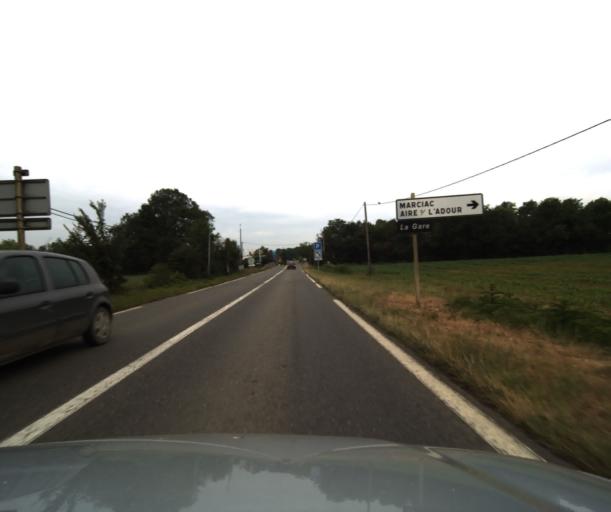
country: FR
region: Midi-Pyrenees
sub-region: Departement du Gers
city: Mielan
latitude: 43.4714
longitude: 0.3303
